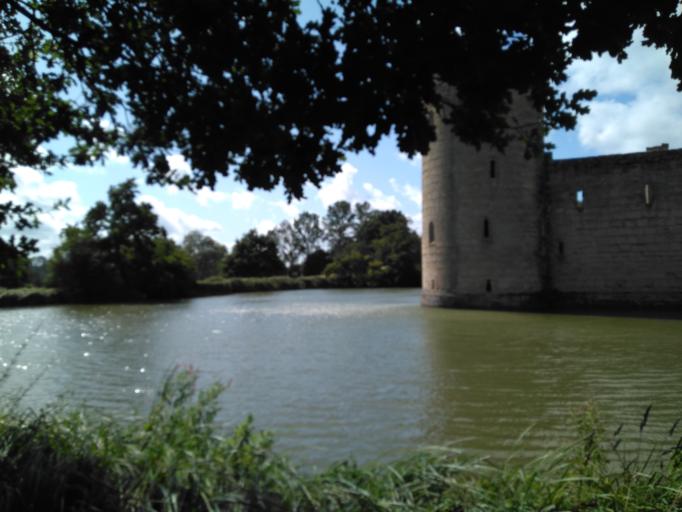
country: GB
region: England
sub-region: East Sussex
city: Northiam
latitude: 51.0021
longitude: 0.5444
